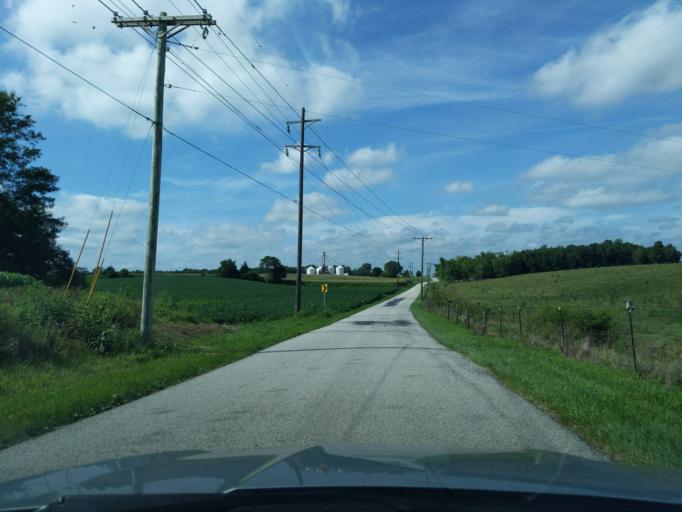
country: US
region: Indiana
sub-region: Ripley County
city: Batesville
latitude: 39.2520
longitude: -85.3475
